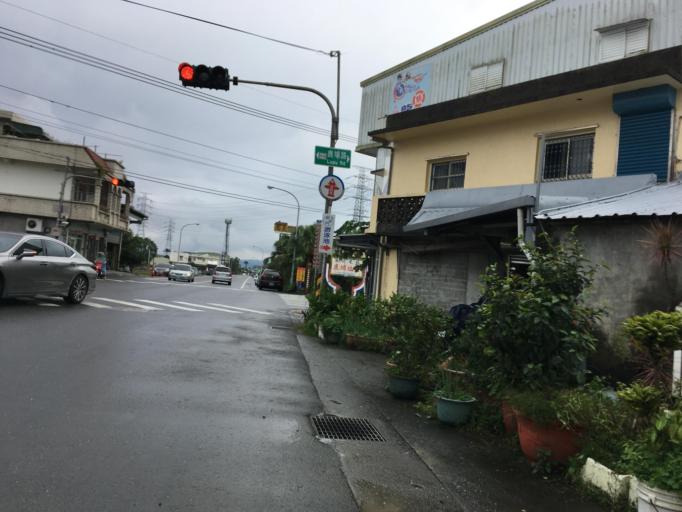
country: TW
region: Taiwan
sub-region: Yilan
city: Yilan
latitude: 24.6608
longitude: 121.7543
